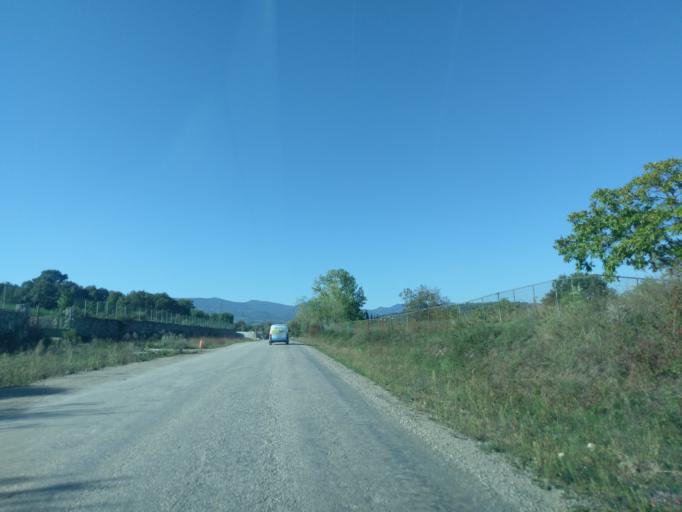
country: TR
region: Sinop
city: Kabali
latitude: 41.8472
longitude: 35.0594
